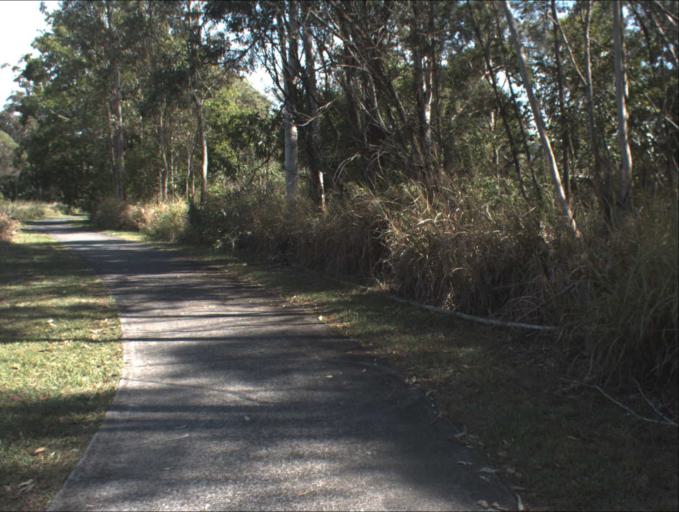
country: AU
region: Queensland
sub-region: Logan
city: Slacks Creek
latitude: -27.6392
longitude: 153.1331
